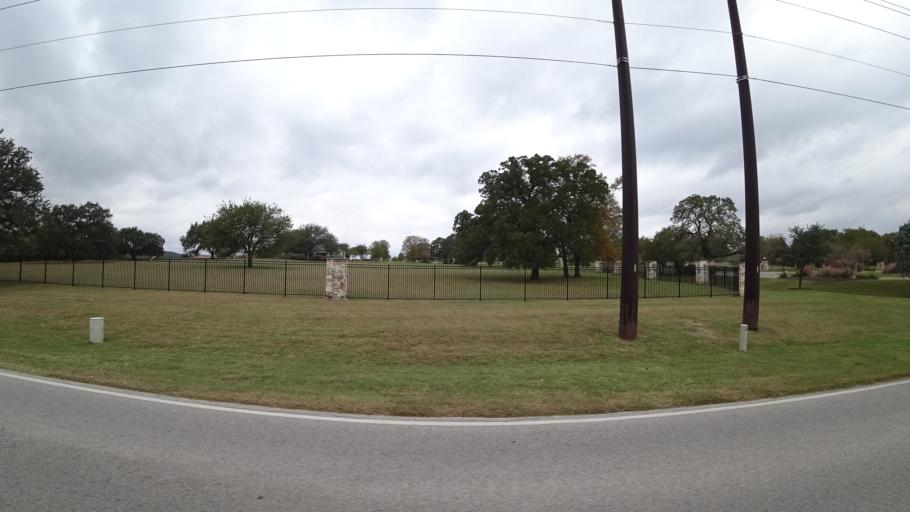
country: US
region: Texas
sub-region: Travis County
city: Bee Cave
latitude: 30.3343
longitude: -97.9231
